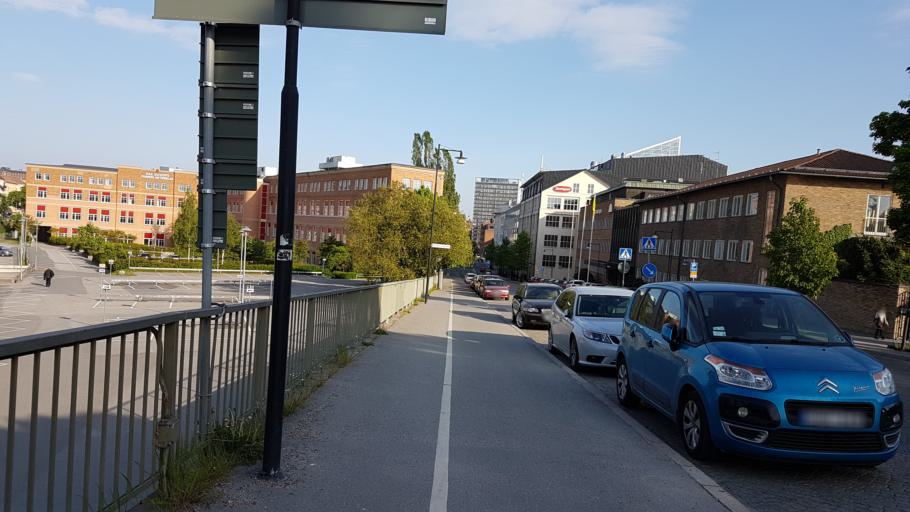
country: SE
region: Stockholm
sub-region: Sundbybergs Kommun
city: Sundbyberg
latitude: 59.3646
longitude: 17.9579
